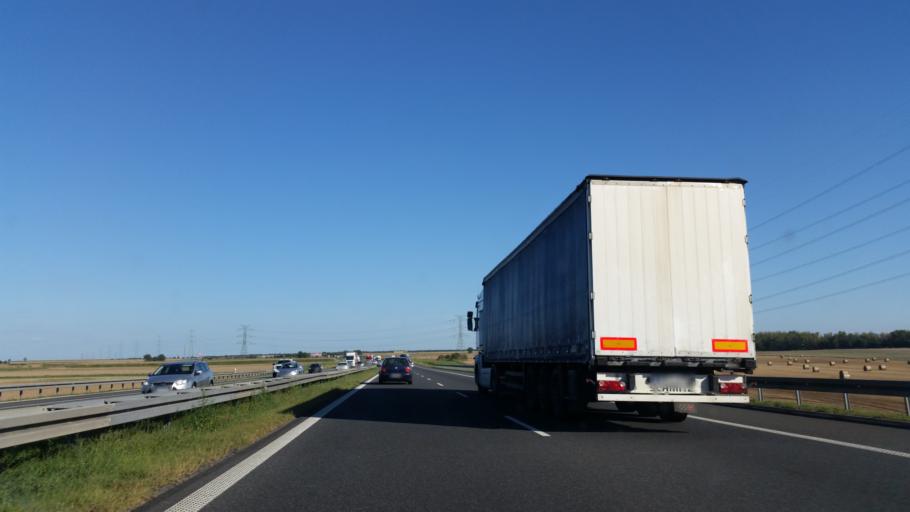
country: PL
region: Opole Voivodeship
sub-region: Powiat brzeski
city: Olszanka
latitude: 50.7472
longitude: 17.4481
